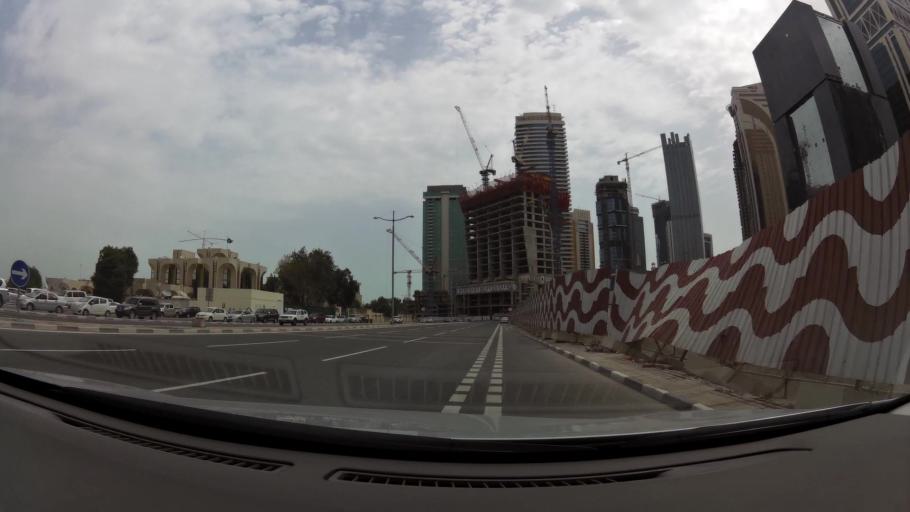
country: QA
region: Baladiyat ad Dawhah
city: Doha
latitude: 25.3303
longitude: 51.5299
